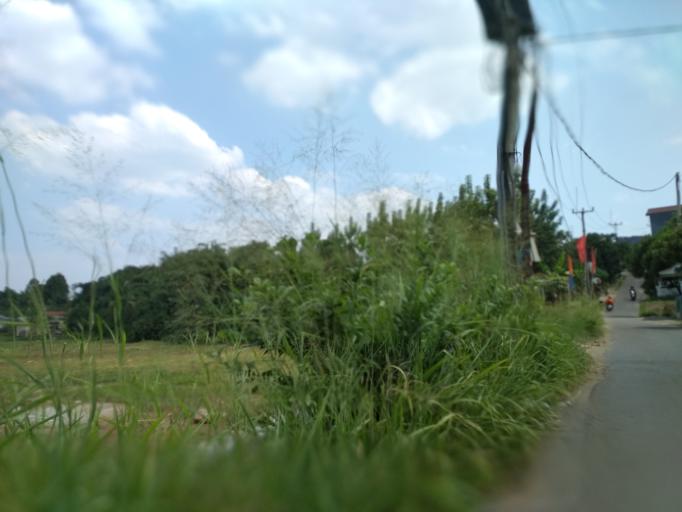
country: ID
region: West Java
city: Ciampea
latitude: -6.5590
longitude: 106.7402
